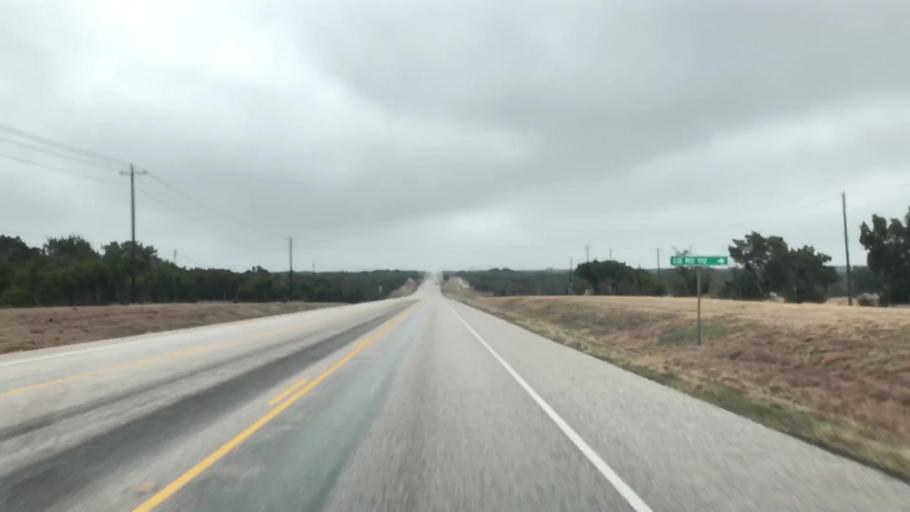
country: US
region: Texas
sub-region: Burnet County
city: Burnet
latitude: 30.8195
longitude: -98.2389
